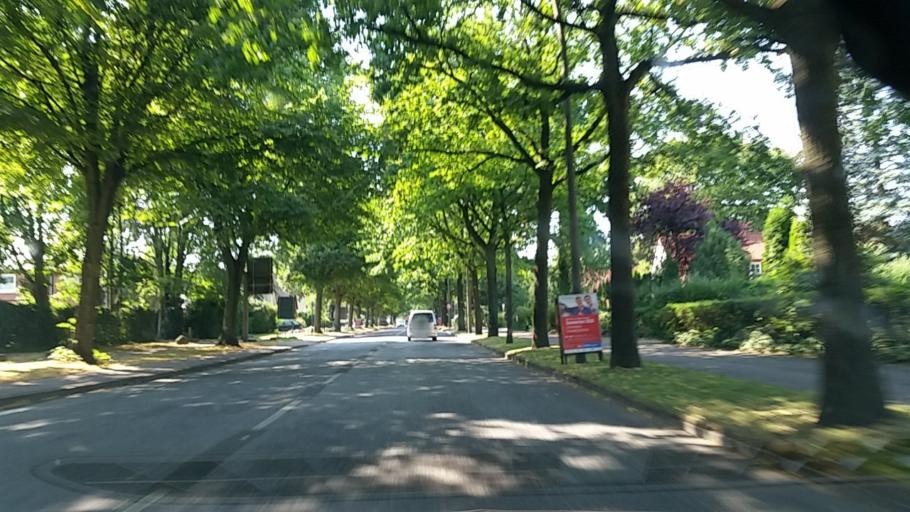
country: DE
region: Hamburg
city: Wandsbek
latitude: 53.5481
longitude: 10.1055
